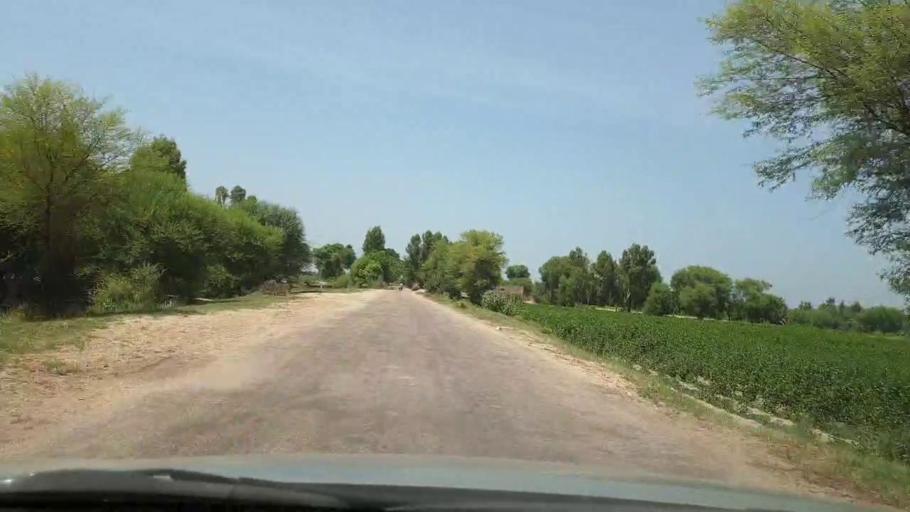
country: PK
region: Sindh
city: Pano Aqil
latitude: 27.6896
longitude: 69.1108
